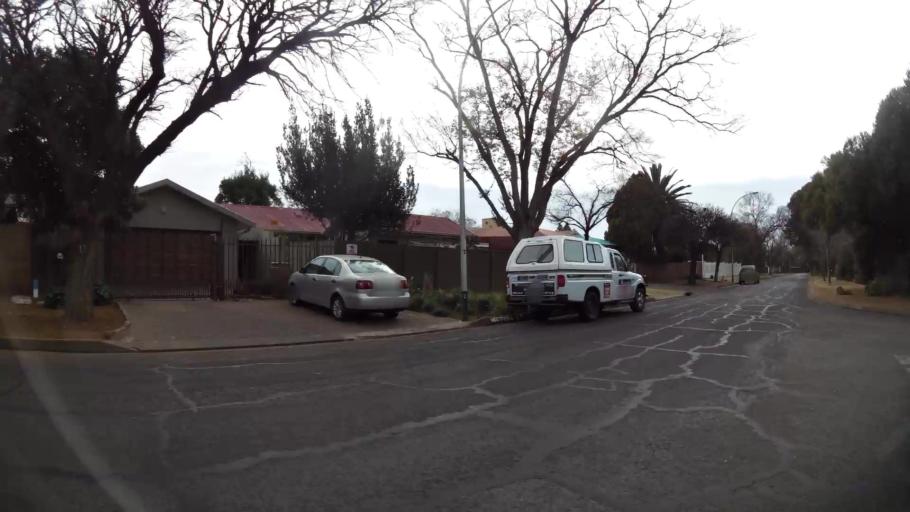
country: ZA
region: Orange Free State
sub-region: Mangaung Metropolitan Municipality
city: Bloemfontein
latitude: -29.1246
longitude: 26.1744
